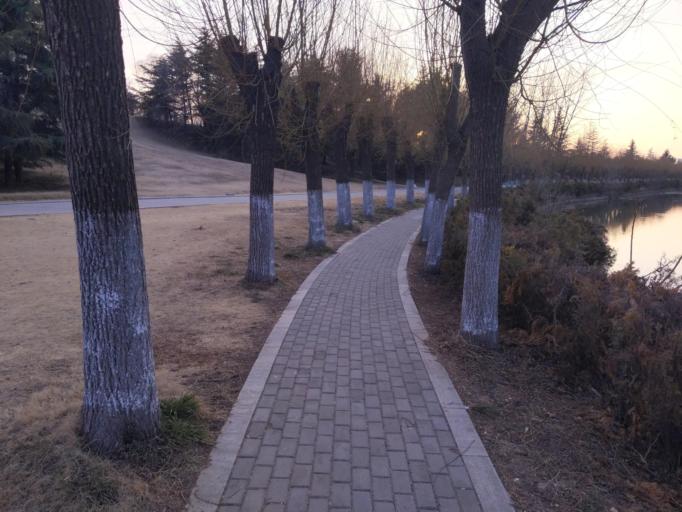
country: CN
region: Henan Sheng
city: Puyang
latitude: 35.7807
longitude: 114.9499
